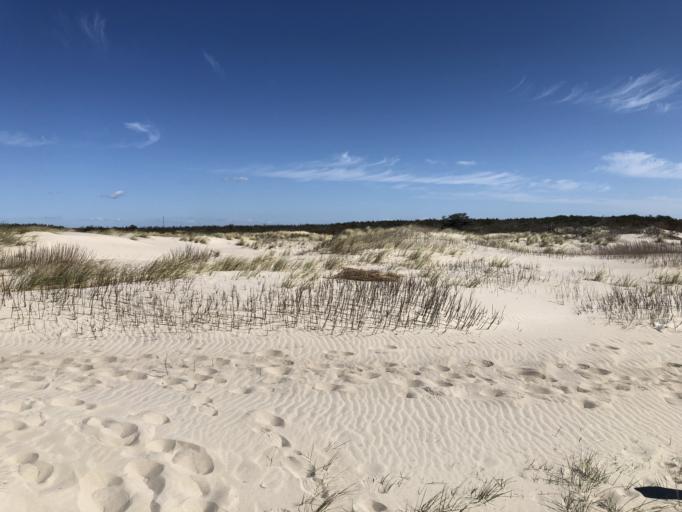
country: DK
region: Central Jutland
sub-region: Holstebro Kommune
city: Ulfborg
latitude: 56.3093
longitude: 8.1267
